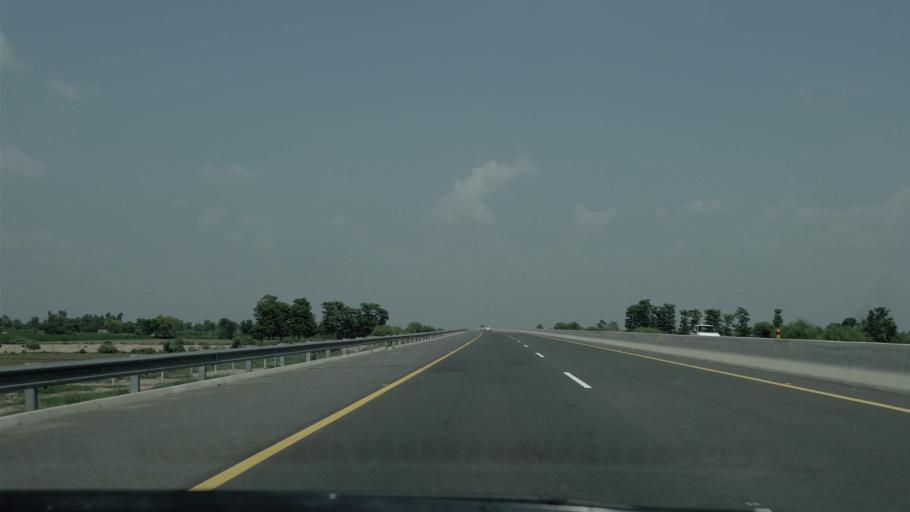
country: PK
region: Punjab
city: Gojra
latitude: 31.1923
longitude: 72.6510
